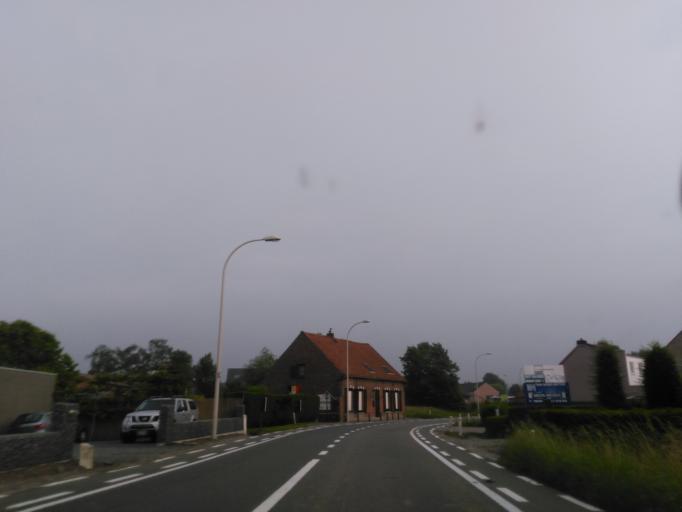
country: BE
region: Flanders
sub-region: Provincie Oost-Vlaanderen
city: Beveren
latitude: 51.2334
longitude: 4.2706
